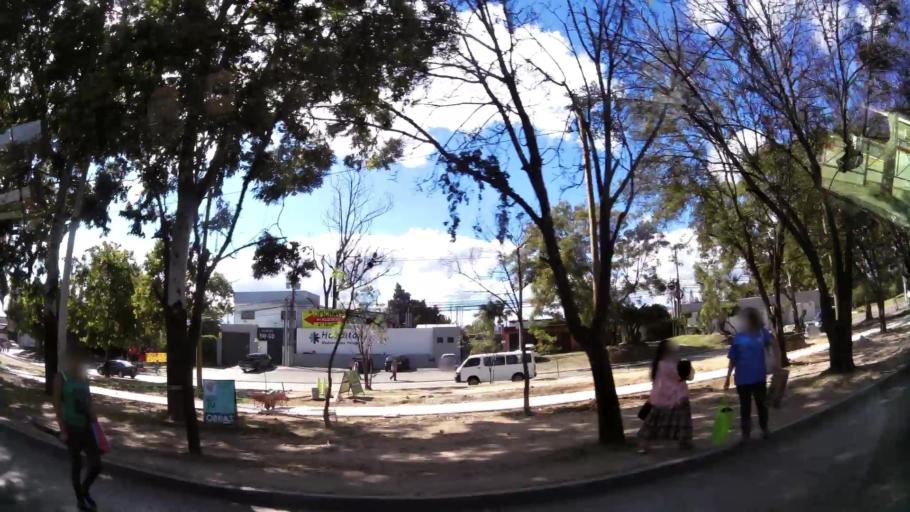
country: GT
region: Guatemala
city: Villa Nueva
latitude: 14.5617
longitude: -90.5503
